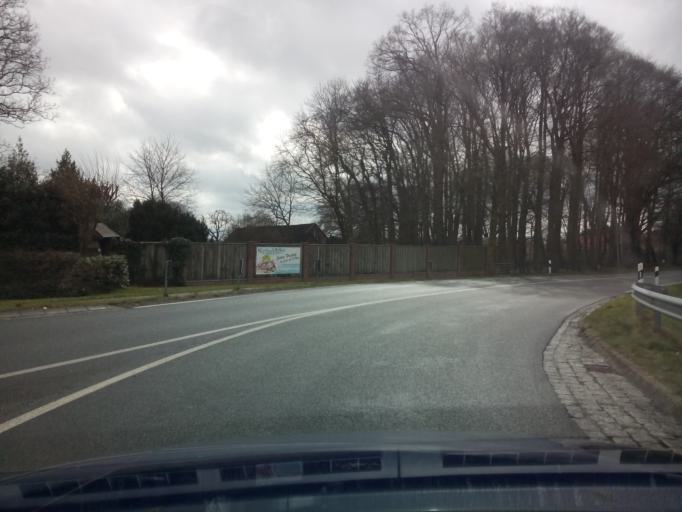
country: DE
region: Lower Saxony
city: Ganderkesee
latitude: 53.0304
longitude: 8.5794
